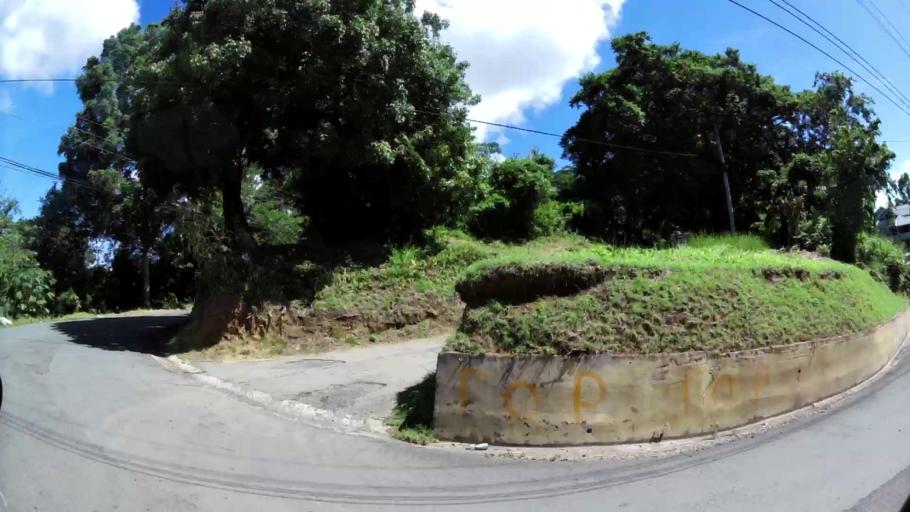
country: TT
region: Tobago
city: Scarborough
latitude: 11.1871
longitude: -60.7802
